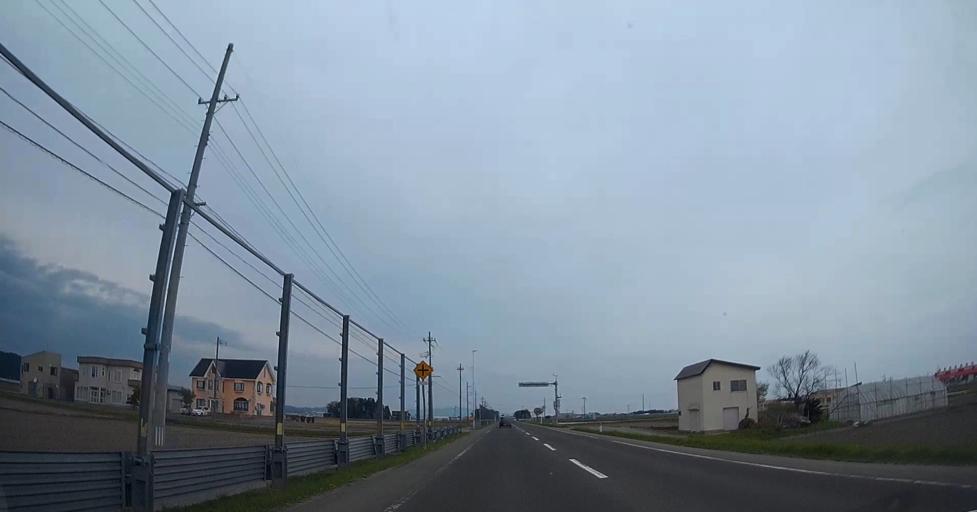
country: JP
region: Aomori
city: Aomori Shi
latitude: 40.8871
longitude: 140.6697
